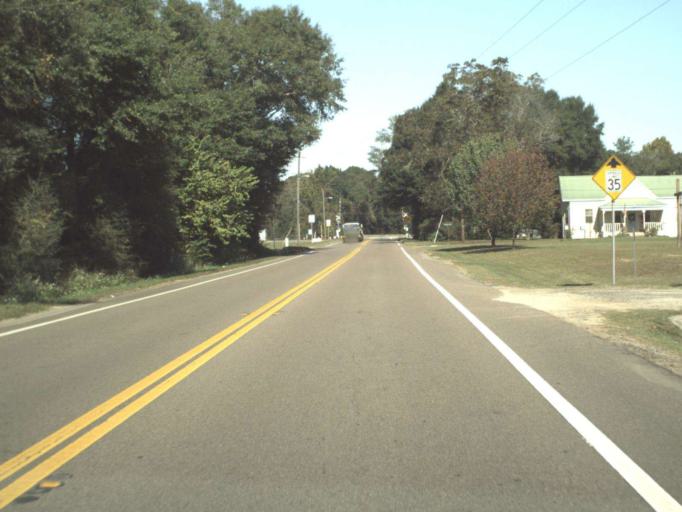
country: US
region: Florida
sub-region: Walton County
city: DeFuniak Springs
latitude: 30.7215
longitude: -85.9368
